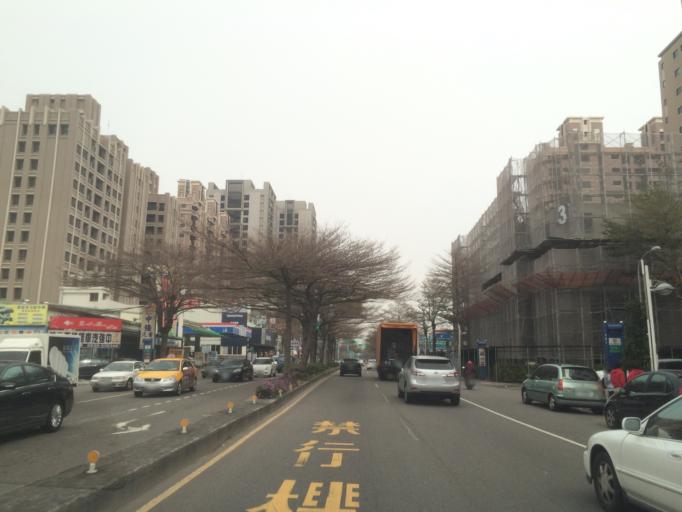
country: TW
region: Taiwan
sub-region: Taichung City
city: Taichung
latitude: 24.1937
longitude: 120.6865
